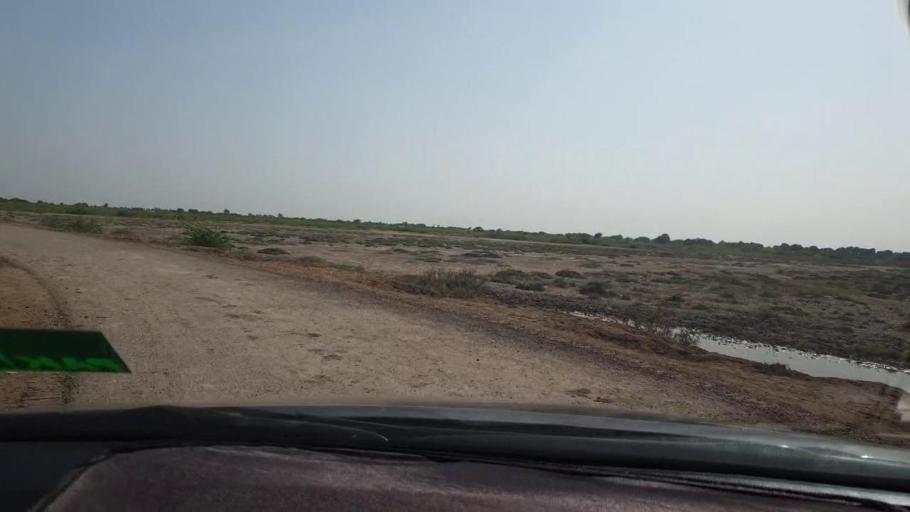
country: PK
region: Sindh
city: Naukot
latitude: 24.9410
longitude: 69.2447
